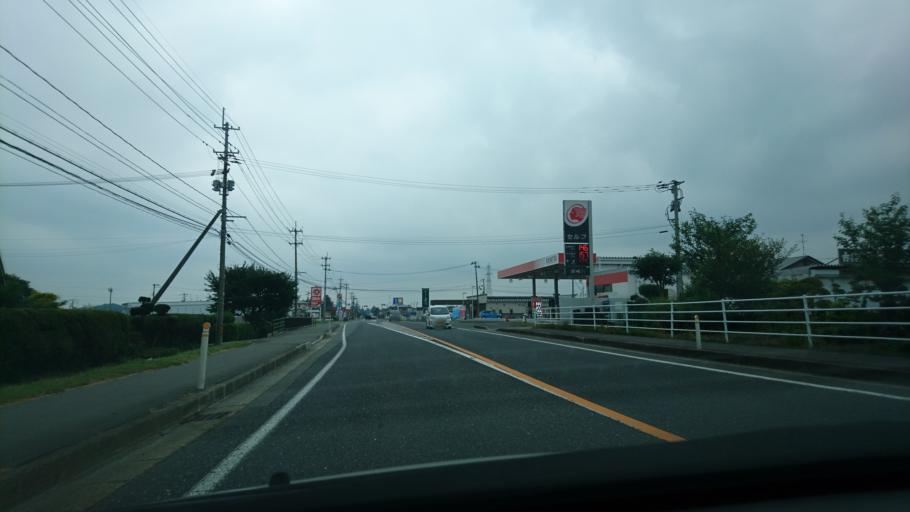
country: JP
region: Miyagi
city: Furukawa
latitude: 38.6433
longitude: 140.8800
